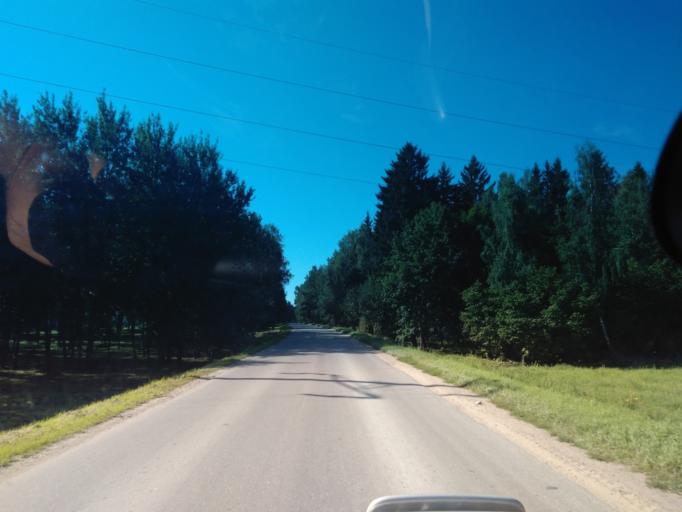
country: BY
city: Fanipol
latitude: 53.7404
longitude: 27.3452
